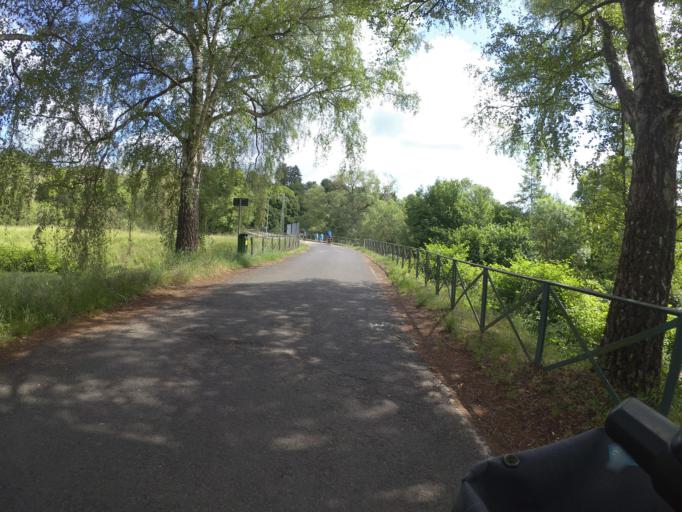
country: DE
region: Rheinland-Pfalz
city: Rehborn
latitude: 49.7359
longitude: 7.6896
